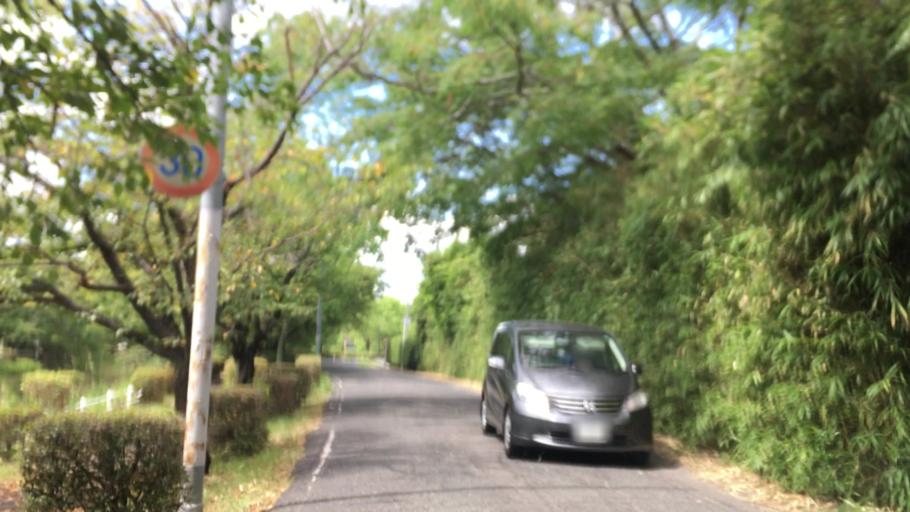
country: JP
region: Saga Prefecture
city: Saga-shi
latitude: 33.2700
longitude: 130.2827
